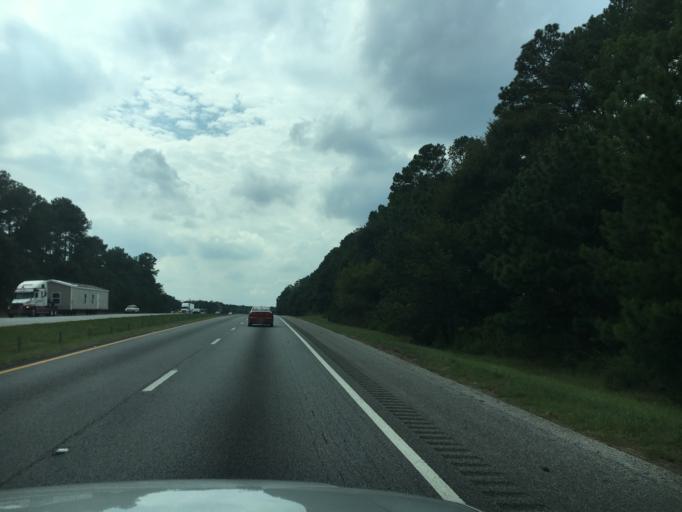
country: US
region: Georgia
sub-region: Hart County
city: Reed Creek
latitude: 34.5187
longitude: -82.8687
